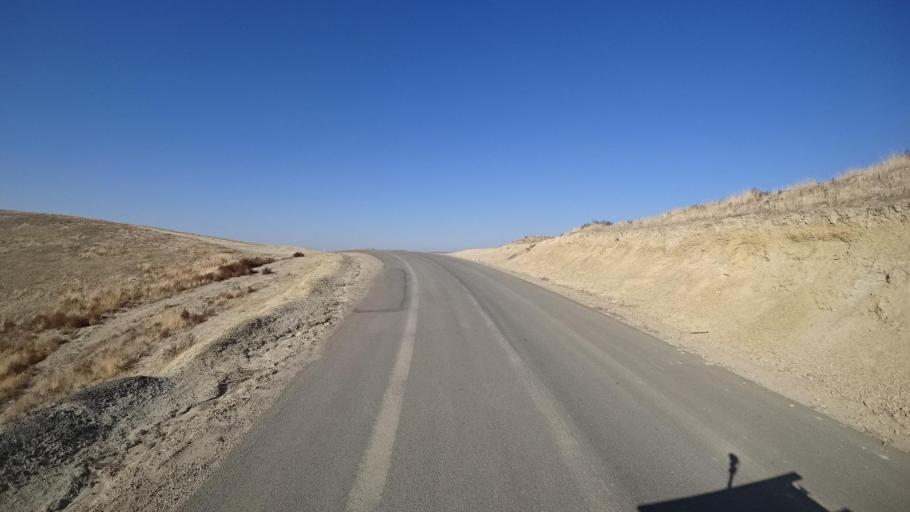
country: US
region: California
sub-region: Kern County
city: Oildale
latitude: 35.4736
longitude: -118.8714
